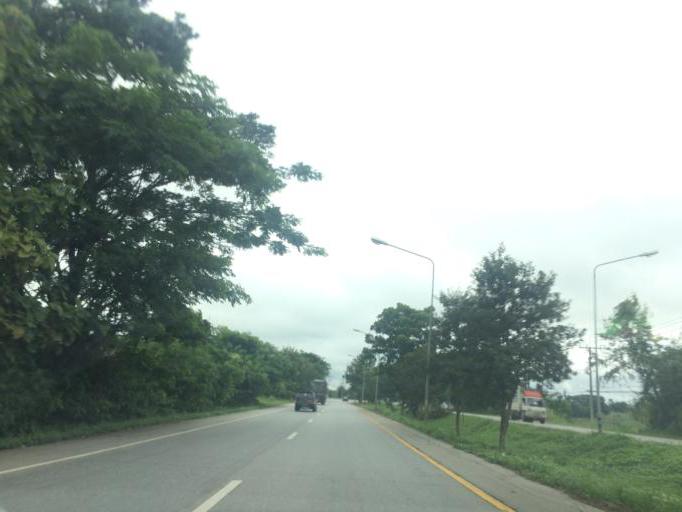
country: TH
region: Chiang Rai
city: Mae Lao
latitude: 19.7918
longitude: 99.7481
